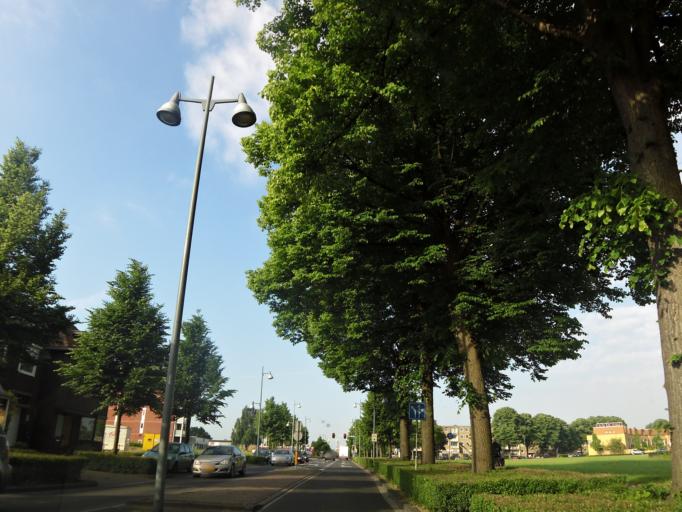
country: NL
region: Limburg
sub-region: Gemeente Sittard-Geleen
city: Limbricht
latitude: 50.9798
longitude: 5.8418
